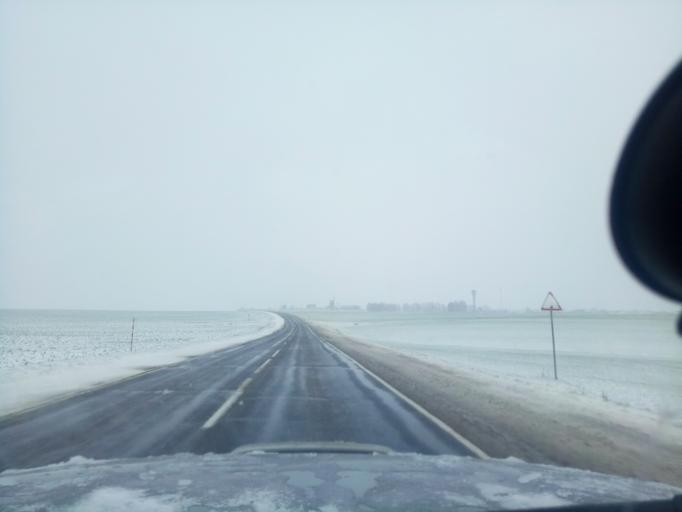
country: BY
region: Minsk
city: Haradzyeya
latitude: 53.3256
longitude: 26.5526
